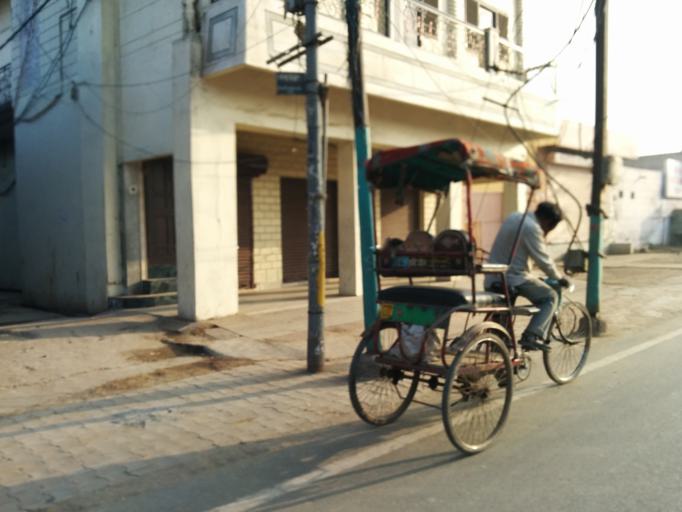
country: IN
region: Uttar Pradesh
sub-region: Mathura
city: Mathura
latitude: 27.5119
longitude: 77.6728
